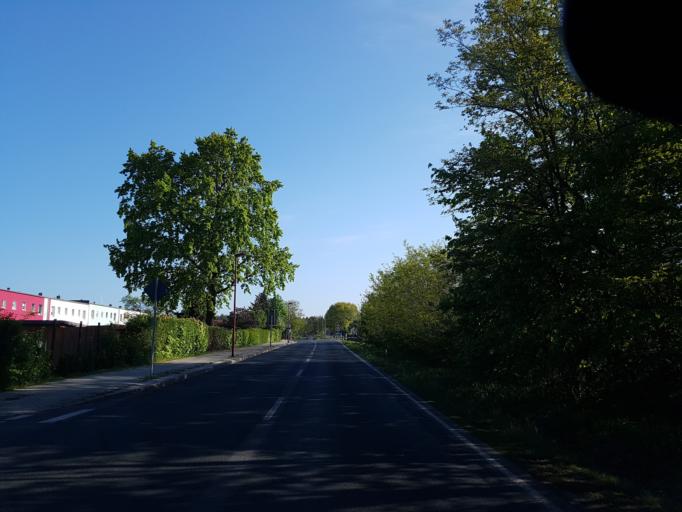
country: DE
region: Brandenburg
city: Grossraschen
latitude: 51.5962
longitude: 14.0142
